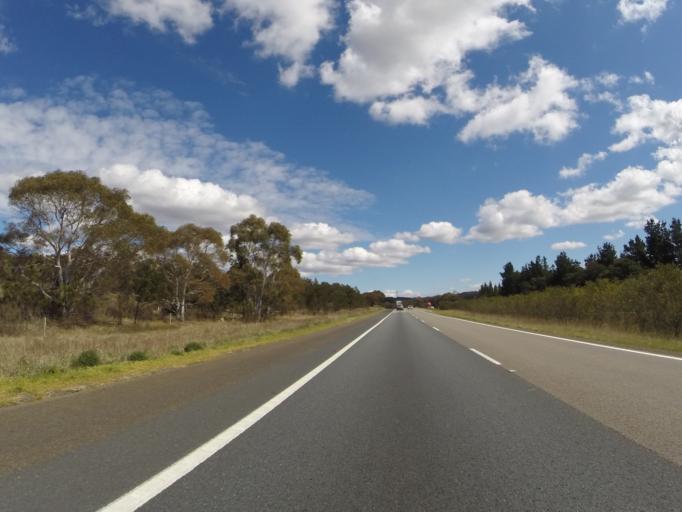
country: AU
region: New South Wales
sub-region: Goulburn Mulwaree
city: Goulburn
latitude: -34.7355
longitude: 149.9552
